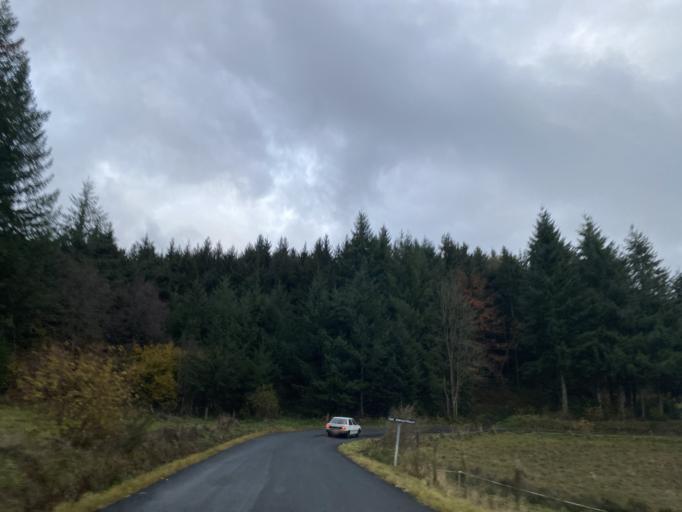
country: FR
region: Auvergne
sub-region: Departement du Puy-de-Dome
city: Cunlhat
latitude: 45.5756
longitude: 3.5610
